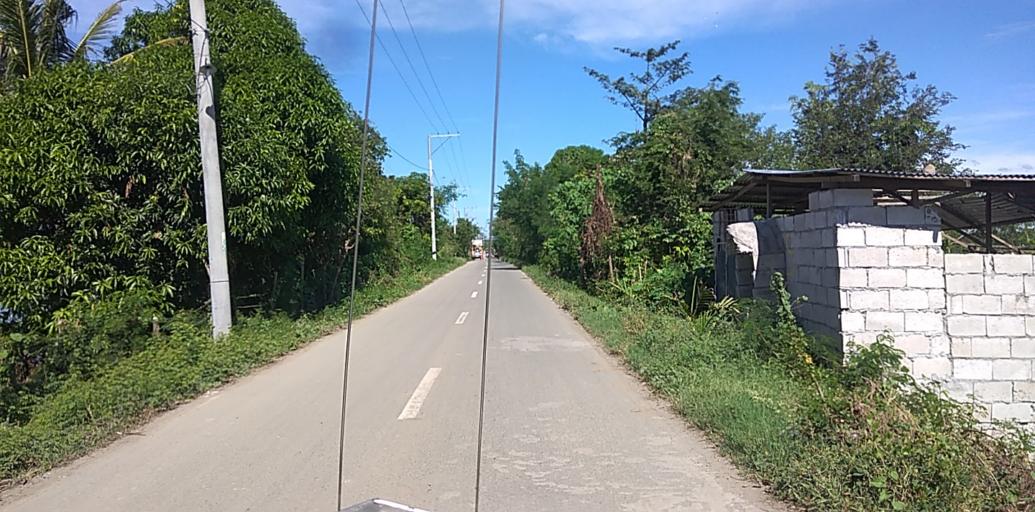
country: PH
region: Central Luzon
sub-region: Province of Pampanga
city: Candaba
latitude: 15.1171
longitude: 120.8144
